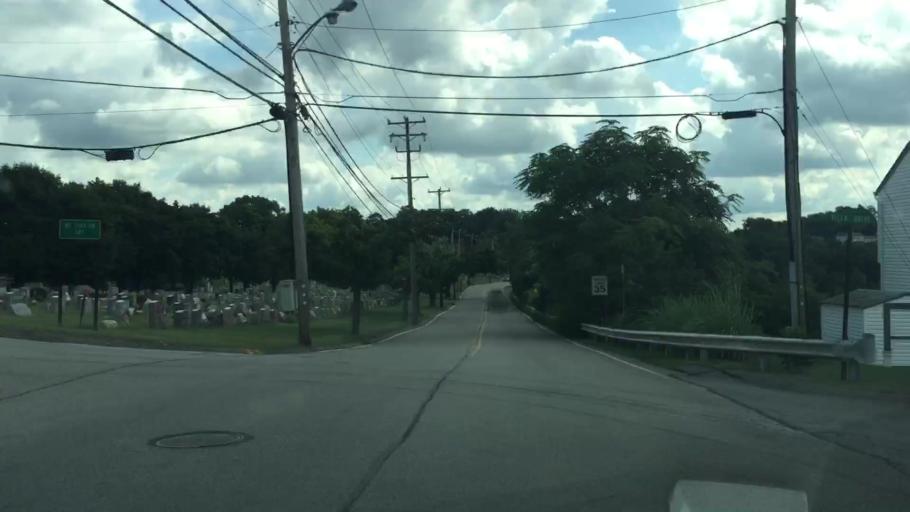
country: US
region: Pennsylvania
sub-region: Allegheny County
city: Millvale
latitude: 40.4958
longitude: -80.0010
